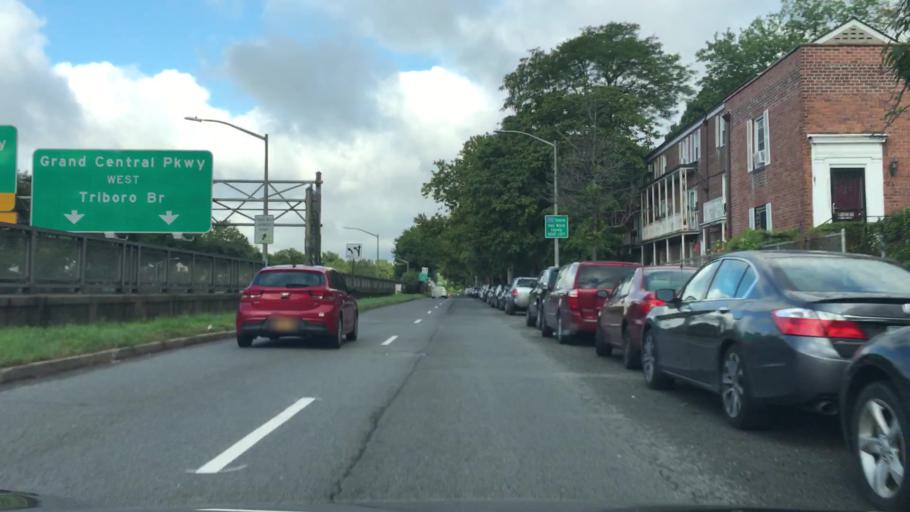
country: US
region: New York
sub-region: Queens County
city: Jamaica
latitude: 40.7160
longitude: -73.8127
